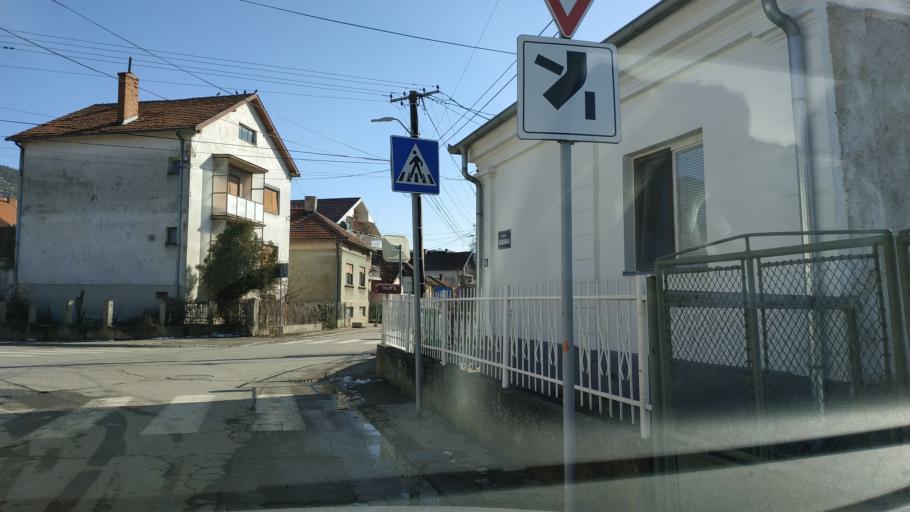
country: RS
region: Central Serbia
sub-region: Nisavski Okrug
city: Aleksinac
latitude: 43.5438
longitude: 21.7110
